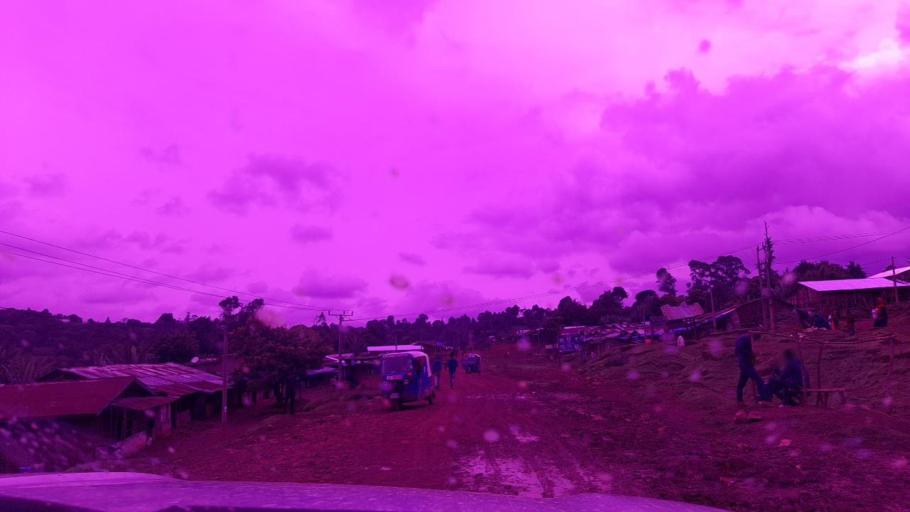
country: ET
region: Southern Nations, Nationalities, and People's Region
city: Tippi
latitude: 7.5679
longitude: 35.6594
